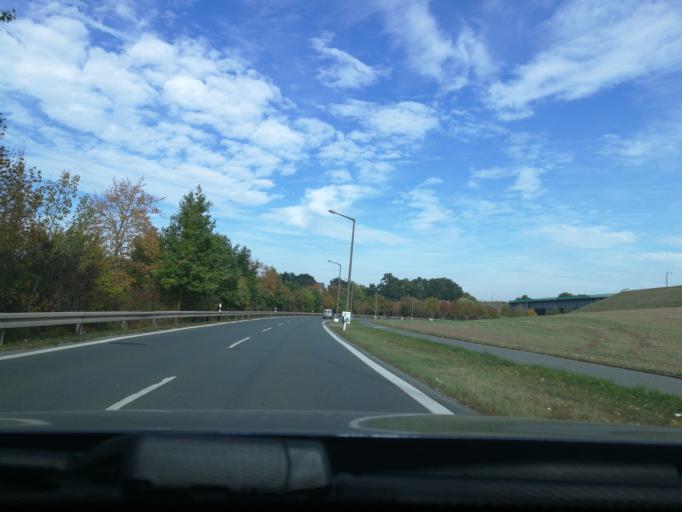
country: DE
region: Bavaria
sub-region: Regierungsbezirk Mittelfranken
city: Furth
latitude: 49.5090
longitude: 10.9575
